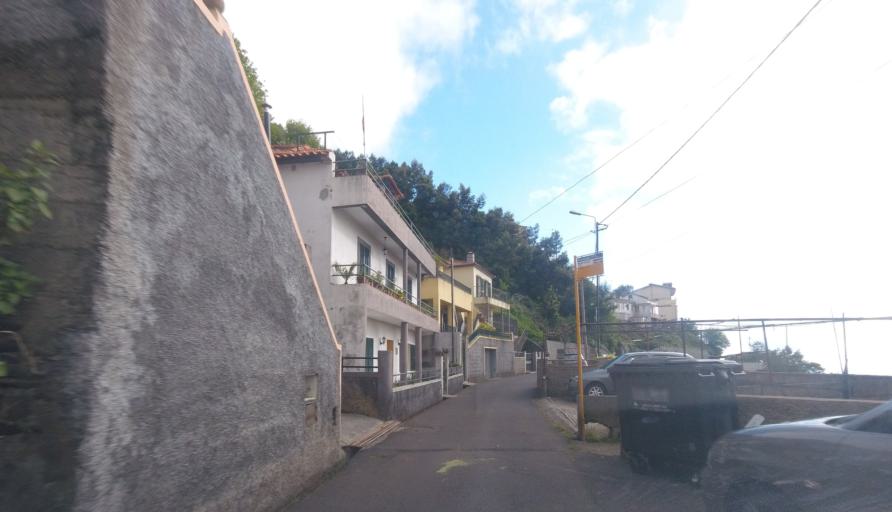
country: PT
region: Madeira
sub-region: Funchal
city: Nossa Senhora do Monte
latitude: 32.6798
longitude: -16.9065
